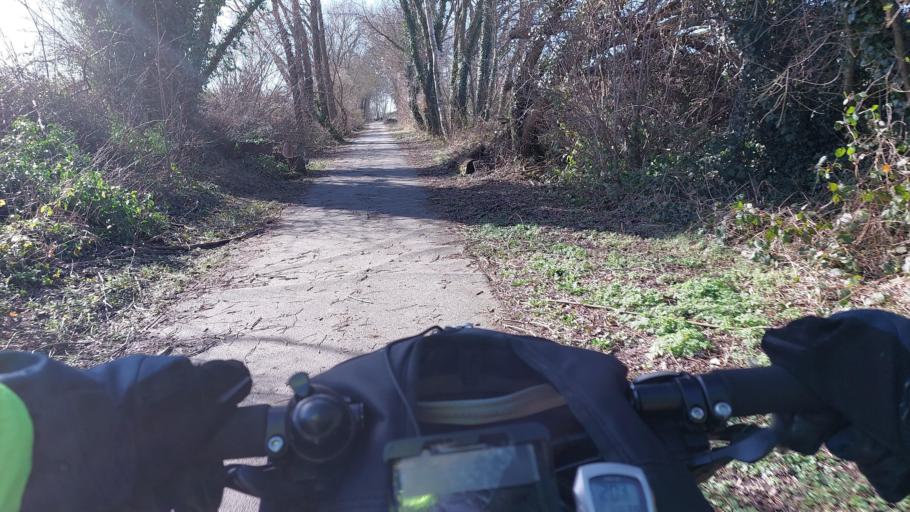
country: BE
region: Wallonia
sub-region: Province du Brabant Wallon
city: Nivelles
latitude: 50.5899
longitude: 4.2916
